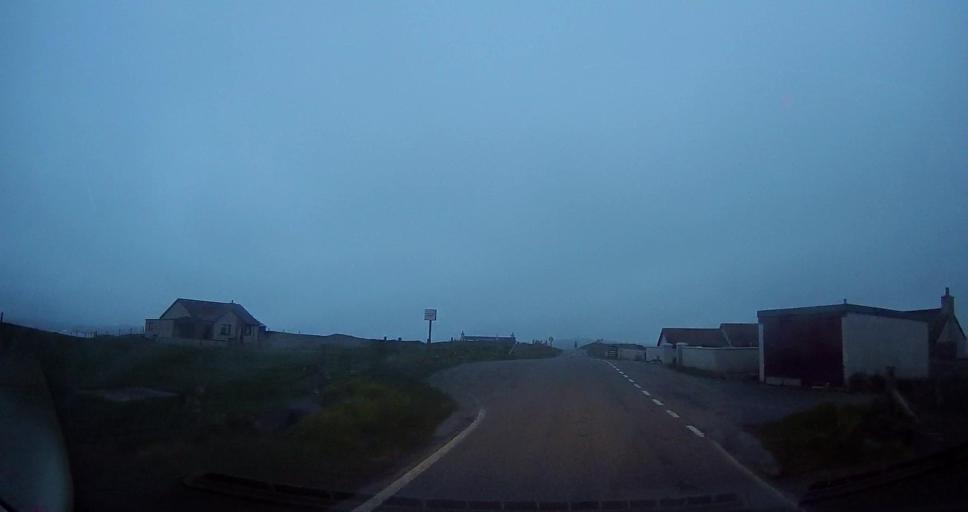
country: GB
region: Scotland
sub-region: Shetland Islands
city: Sandwick
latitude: 60.0153
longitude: -1.2284
